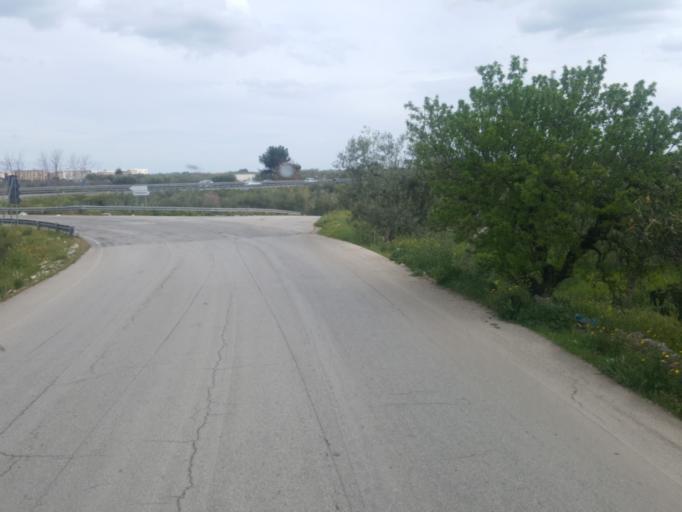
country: IT
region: Apulia
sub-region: Provincia di Barletta - Andria - Trani
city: Bisceglie
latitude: 41.2218
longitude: 16.5065
